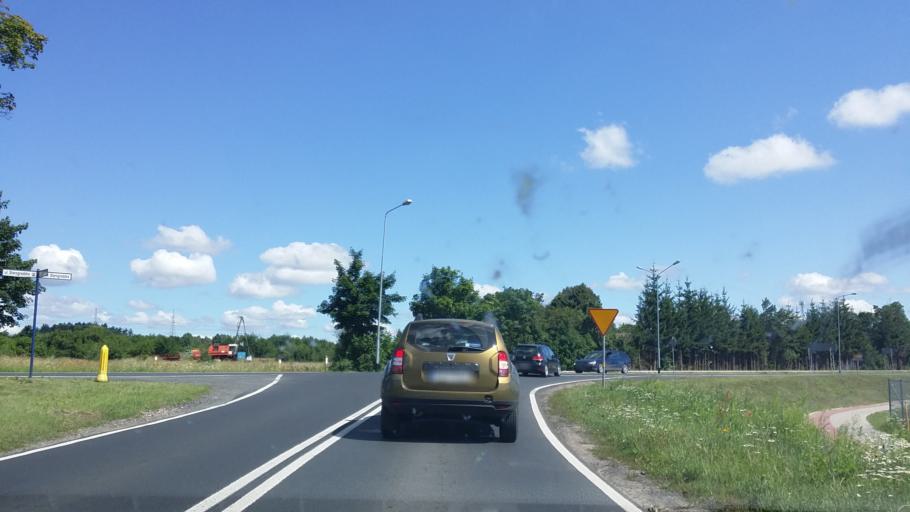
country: PL
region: West Pomeranian Voivodeship
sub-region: Powiat drawski
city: Drawsko Pomorskie
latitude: 53.5223
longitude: 15.7869
